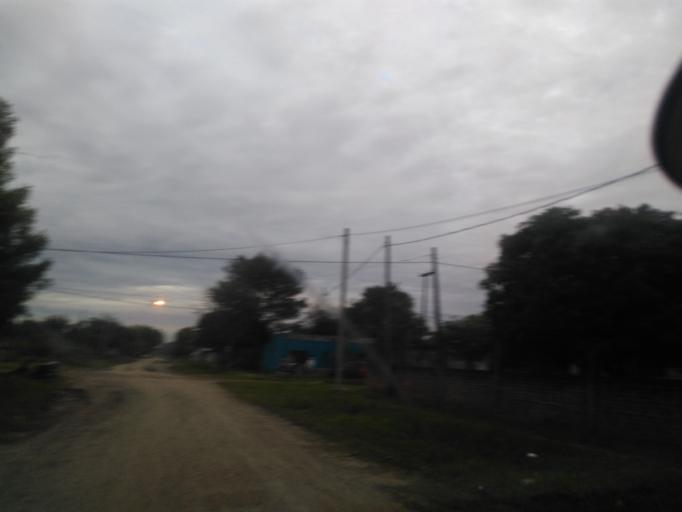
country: AR
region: Chaco
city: Resistencia
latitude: -27.4729
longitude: -59.0125
